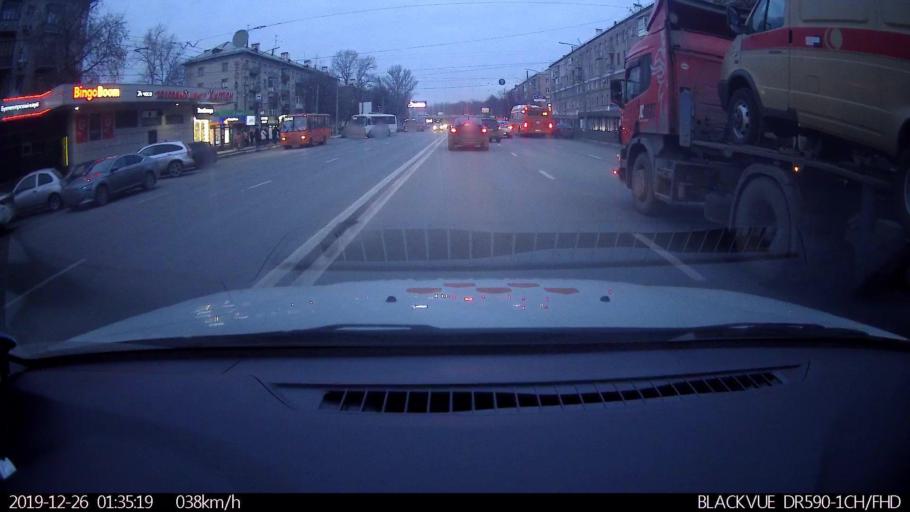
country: RU
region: Nizjnij Novgorod
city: Nizhniy Novgorod
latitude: 56.2652
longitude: 43.9115
